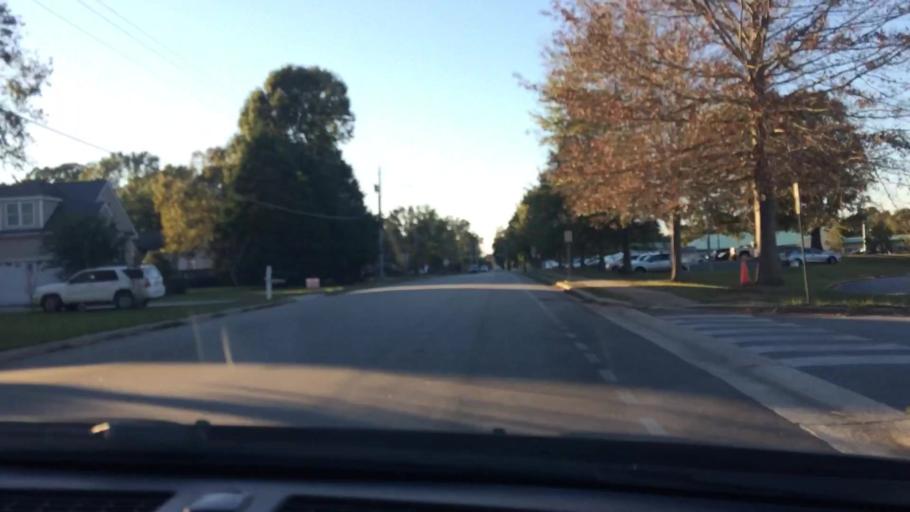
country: US
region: North Carolina
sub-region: Pitt County
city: Farmville
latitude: 35.5933
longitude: -77.5746
